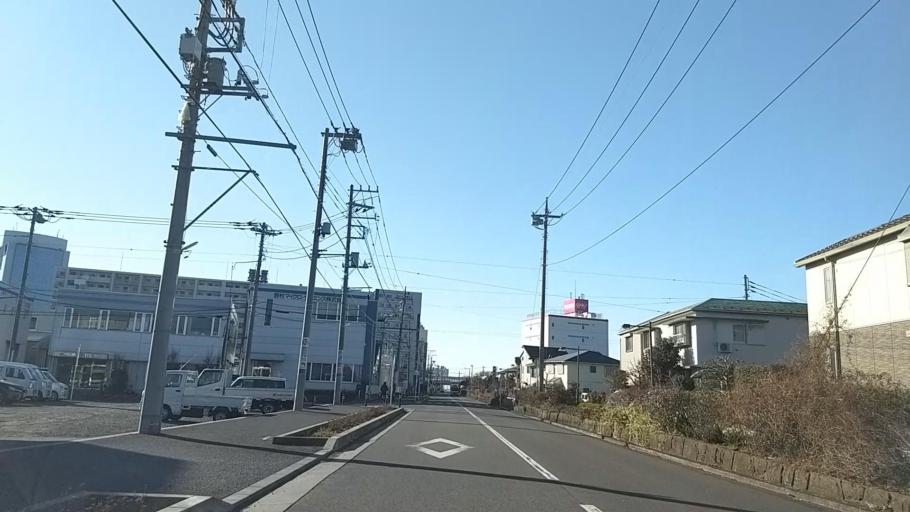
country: JP
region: Kanagawa
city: Atsugi
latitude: 35.4294
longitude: 139.3591
